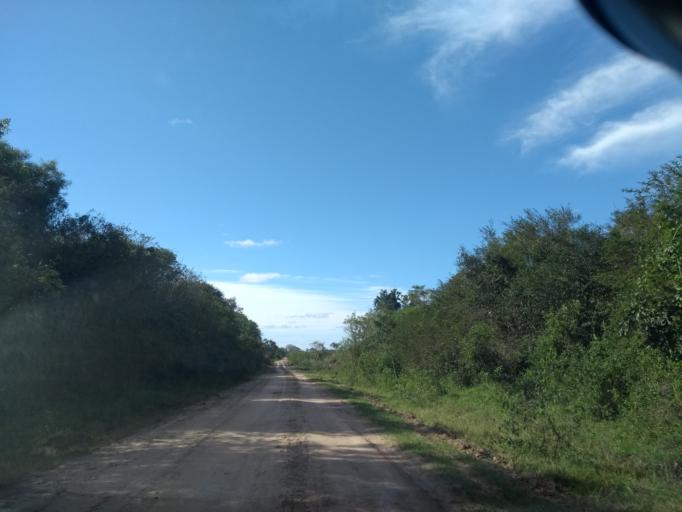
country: AR
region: Chaco
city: Margarita Belen
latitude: -27.2831
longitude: -58.9269
